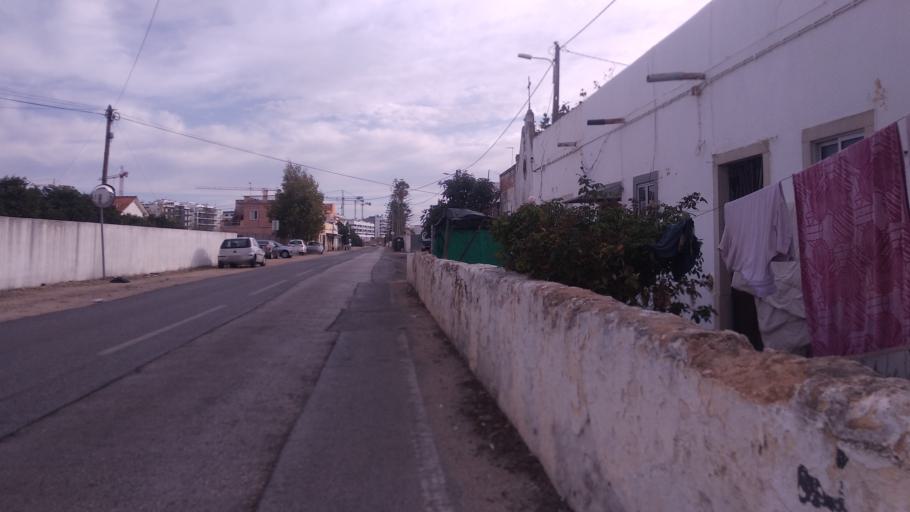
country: PT
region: Faro
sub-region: Faro
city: Faro
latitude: 37.0364
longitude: -7.9403
